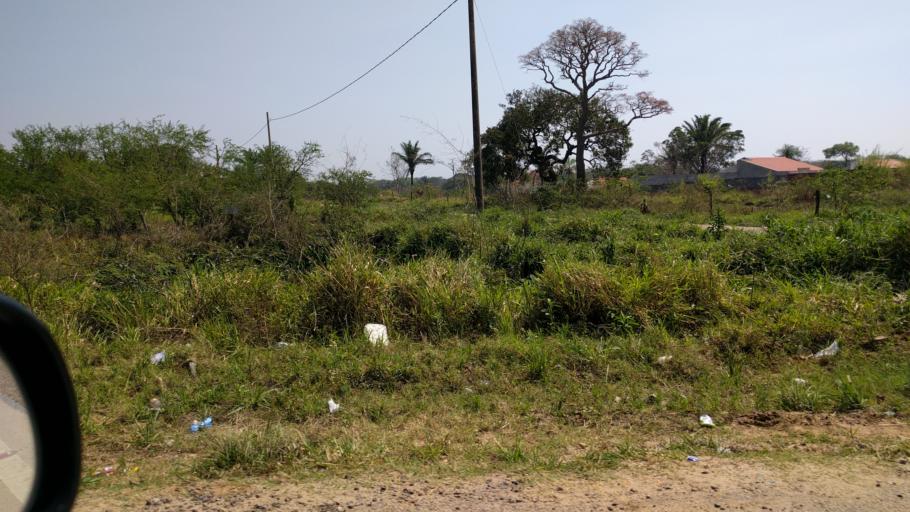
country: BO
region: Santa Cruz
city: Santa Cruz de la Sierra
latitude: -17.7620
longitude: -63.2310
